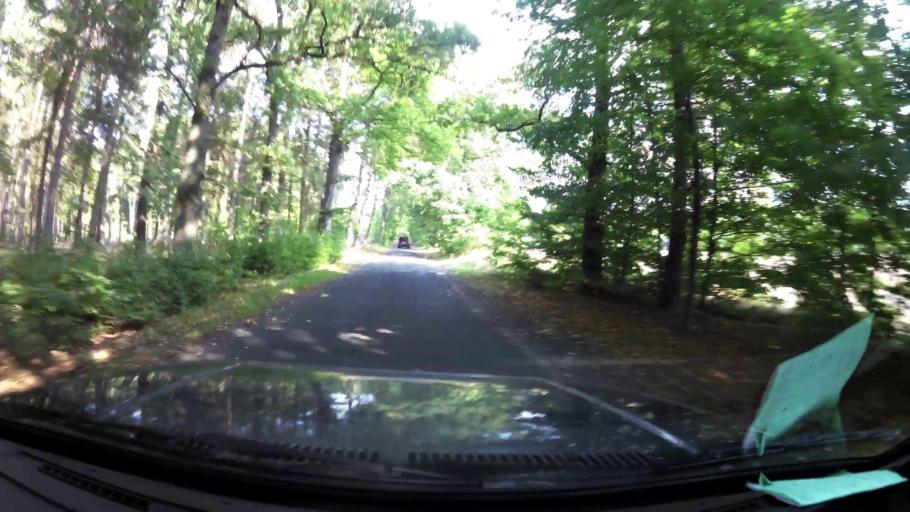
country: PL
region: West Pomeranian Voivodeship
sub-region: Powiat koszalinski
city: Bobolice
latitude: 54.0960
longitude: 16.4890
